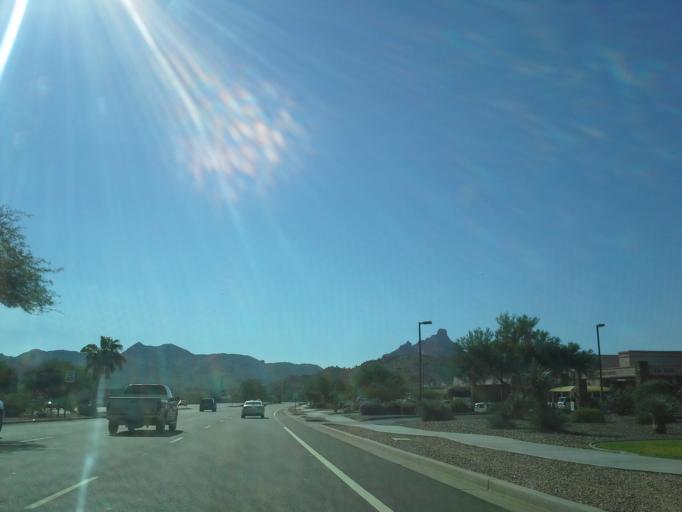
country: US
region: Arizona
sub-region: Maricopa County
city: Fountain Hills
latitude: 33.5724
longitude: -111.7134
